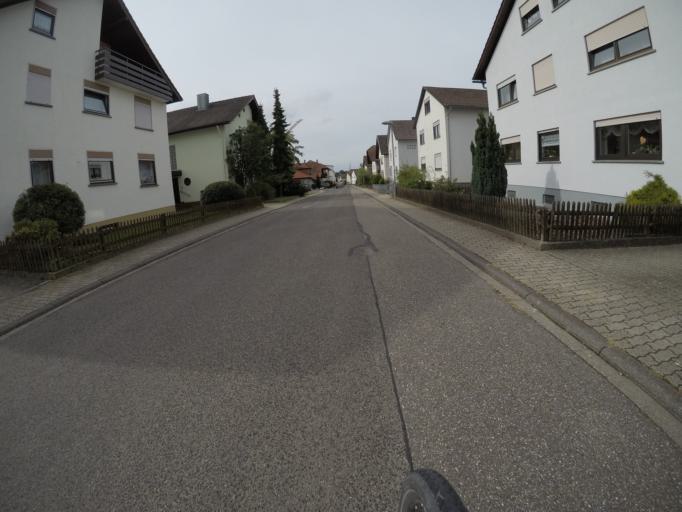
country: DE
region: Baden-Wuerttemberg
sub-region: Karlsruhe Region
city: Ubstadt-Weiher
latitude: 49.1588
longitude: 8.6378
